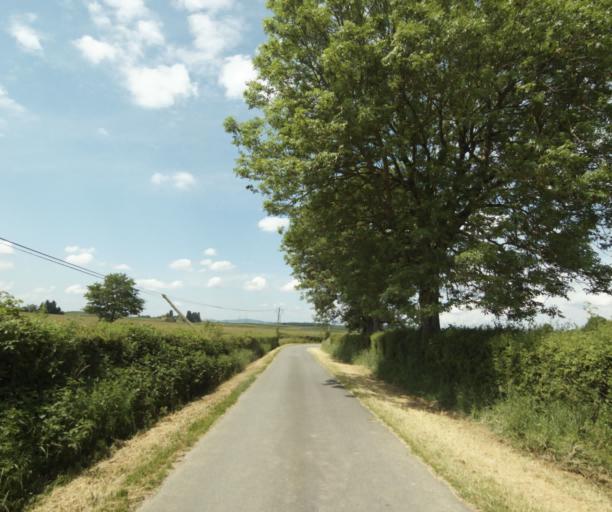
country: FR
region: Bourgogne
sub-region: Departement de Saone-et-Loire
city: Perrecy-les-Forges
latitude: 46.5961
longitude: 4.1412
